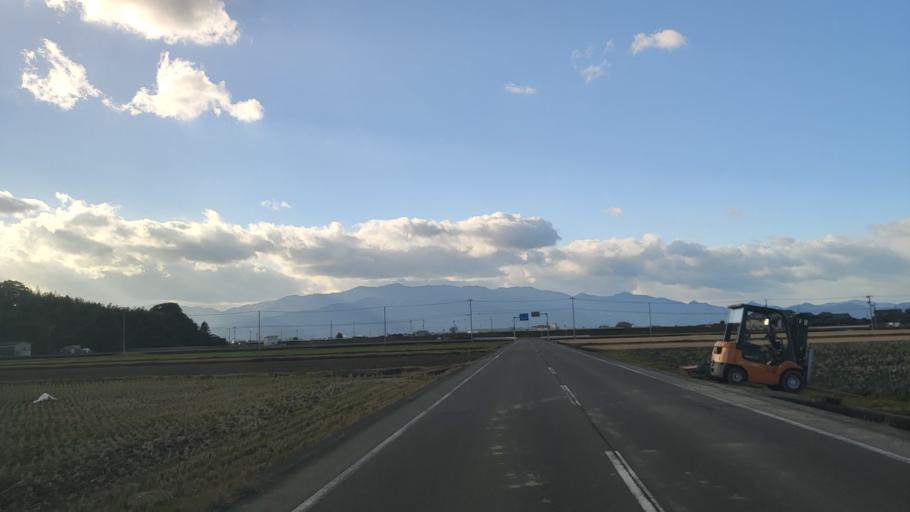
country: JP
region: Ehime
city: Saijo
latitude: 33.9040
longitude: 133.1315
